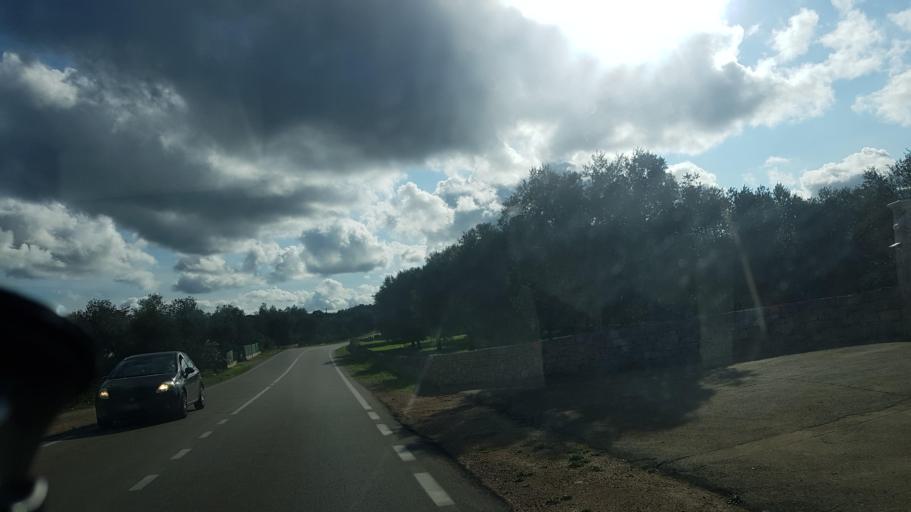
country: IT
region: Apulia
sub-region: Provincia di Brindisi
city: Ostuni
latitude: 40.6838
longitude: 17.5902
